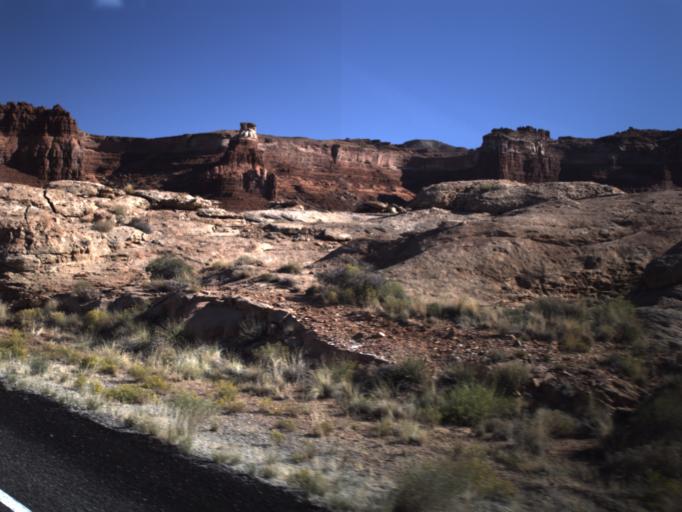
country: US
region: Utah
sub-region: San Juan County
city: Blanding
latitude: 37.9014
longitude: -110.3789
